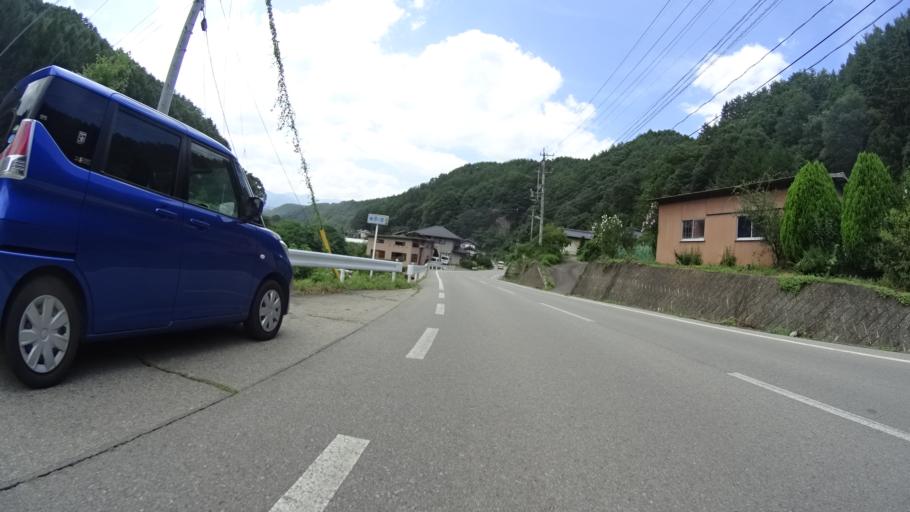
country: JP
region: Nagano
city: Saku
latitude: 36.0608
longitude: 138.5288
